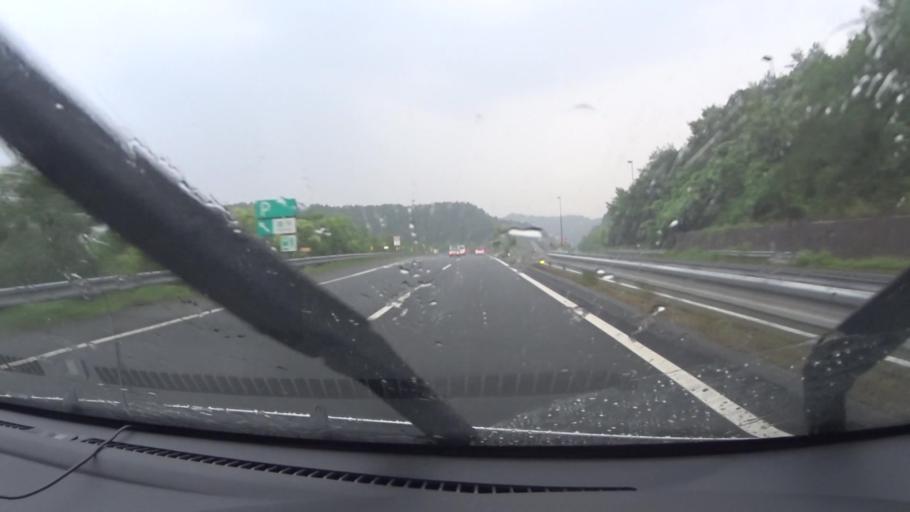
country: JP
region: Kyoto
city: Kameoka
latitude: 35.0819
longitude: 135.5106
